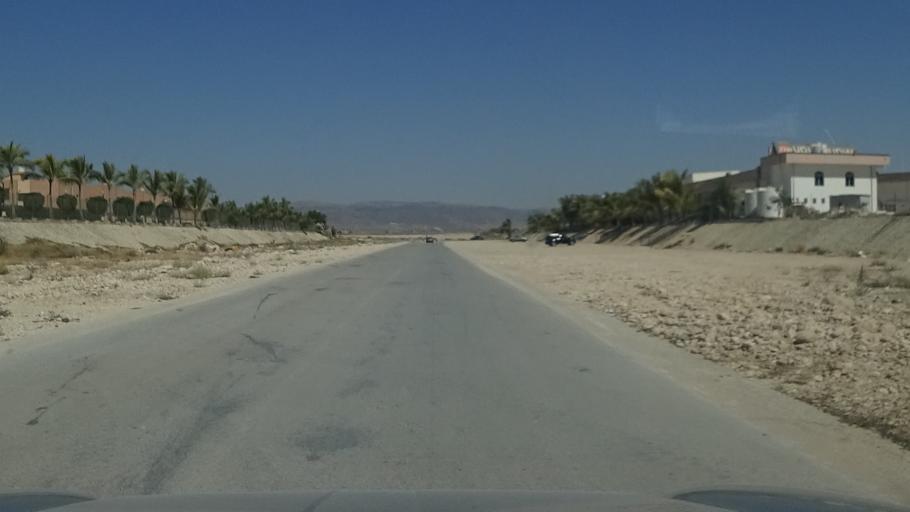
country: OM
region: Zufar
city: Salalah
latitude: 17.0209
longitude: 54.0631
